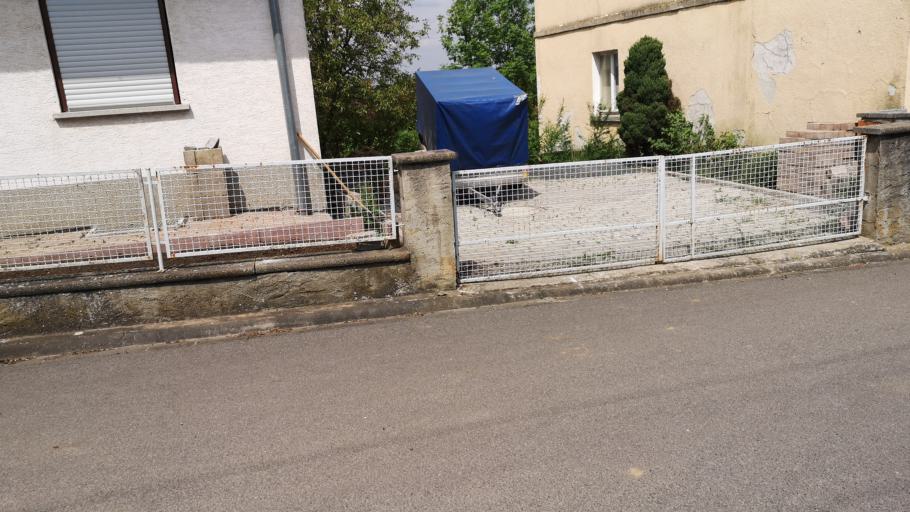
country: DE
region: Bavaria
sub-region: Regierungsbezirk Unterfranken
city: Kolitzheim
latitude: 49.8968
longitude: 10.2710
